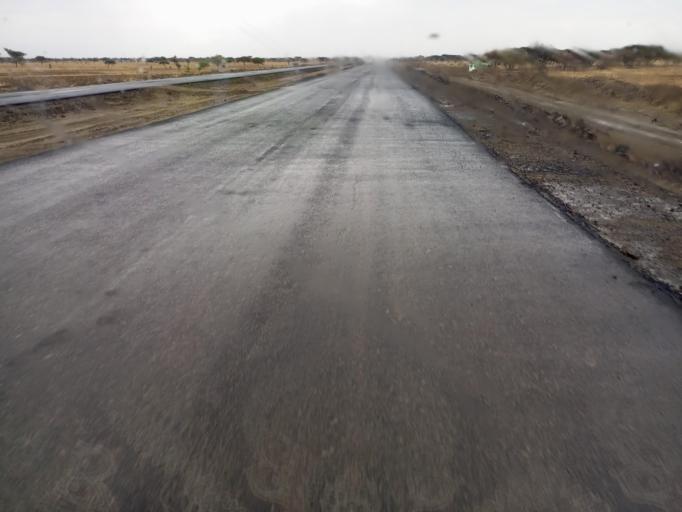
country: ET
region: Oromiya
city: Ziway
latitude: 7.7490
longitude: 38.6151
